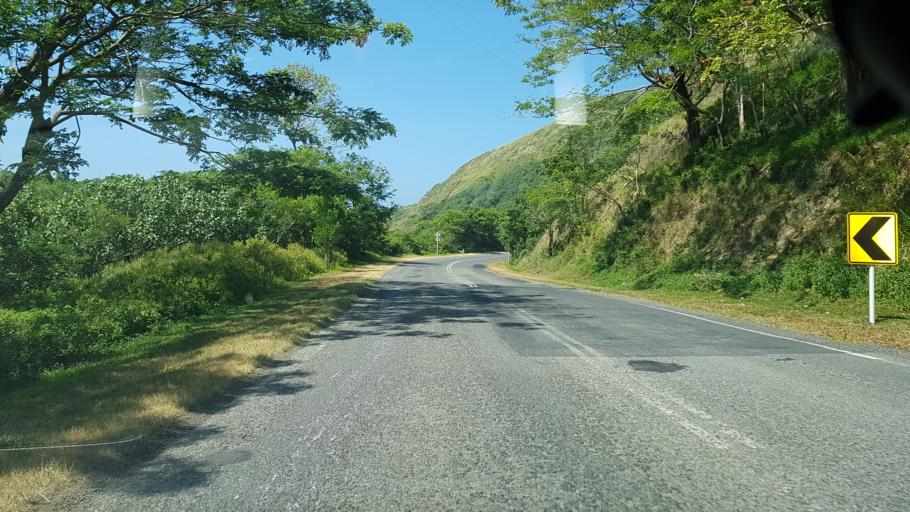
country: FJ
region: Western
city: Nadi
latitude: -18.1740
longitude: 177.5902
